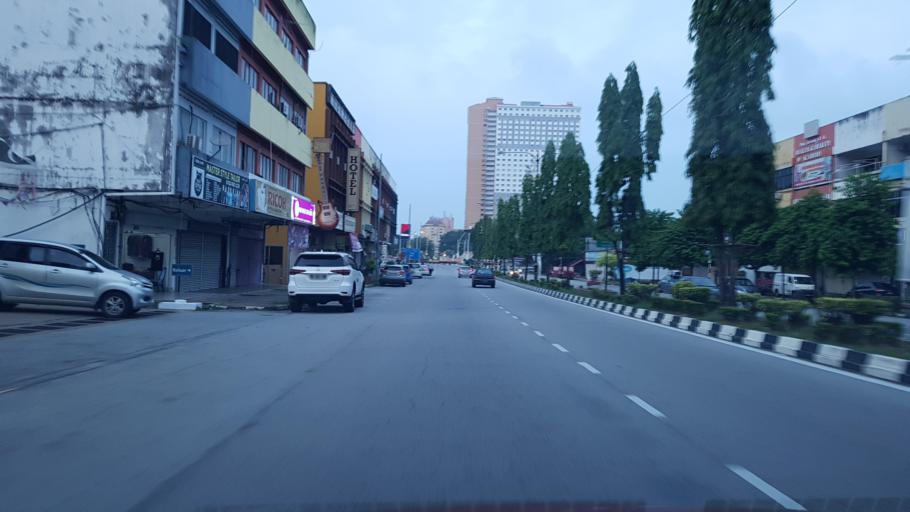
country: MY
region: Terengganu
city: Kuala Terengganu
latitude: 5.3283
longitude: 103.1439
